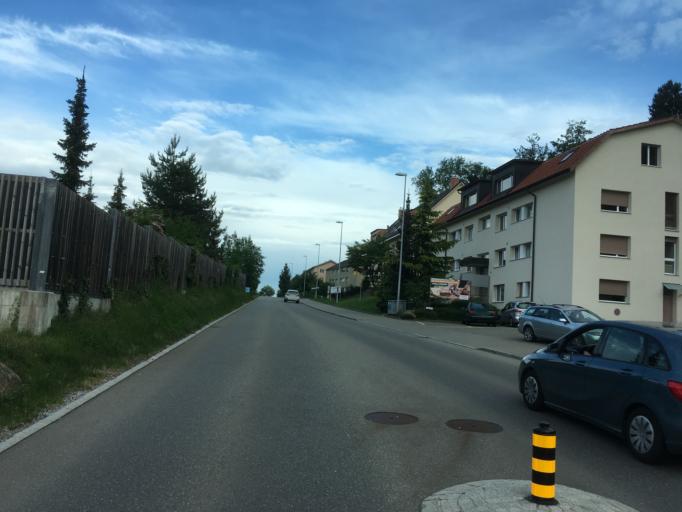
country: CH
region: Zurich
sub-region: Bezirk Uster
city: Pfaffhausen
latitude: 47.3625
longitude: 8.6188
